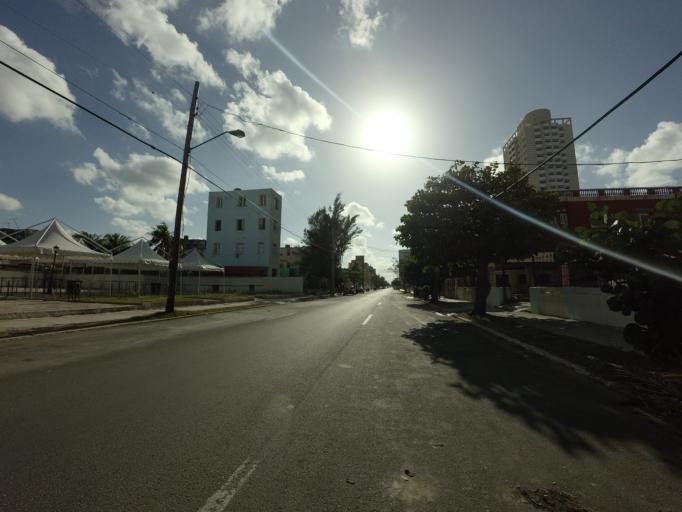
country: CU
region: La Habana
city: Havana
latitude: 23.1430
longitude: -82.3975
